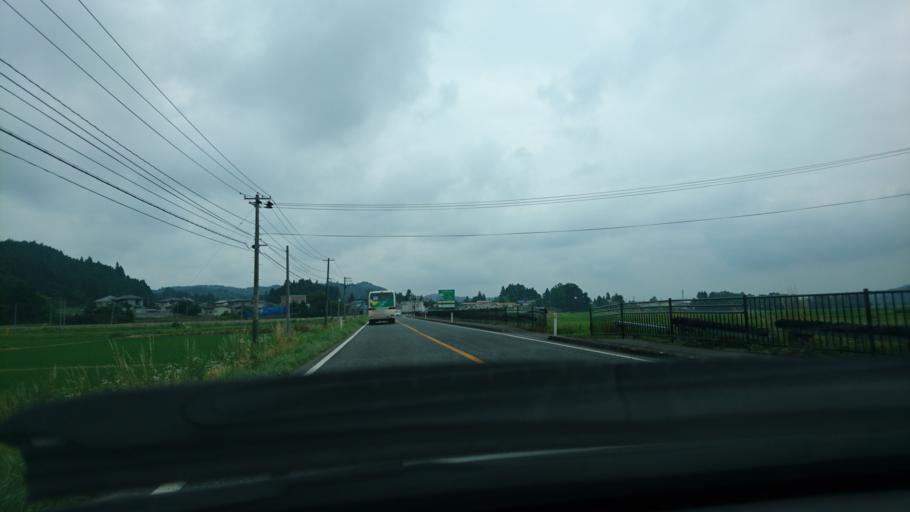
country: JP
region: Miyagi
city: Furukawa
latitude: 38.7143
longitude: 140.8270
